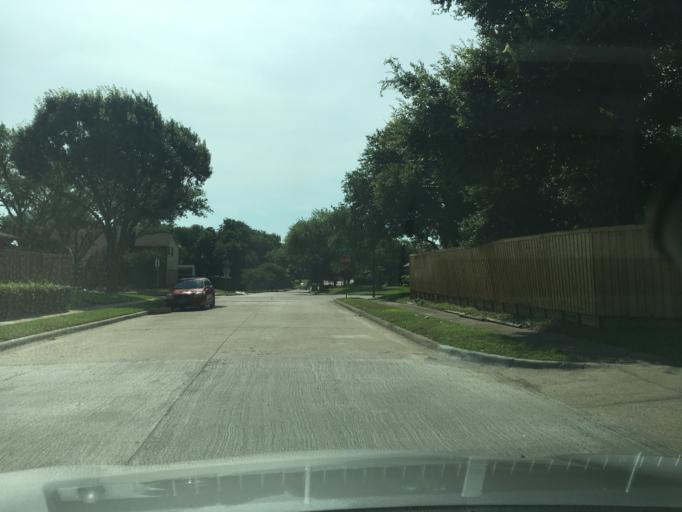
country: US
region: Texas
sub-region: Dallas County
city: Richardson
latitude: 32.9651
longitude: -96.6801
